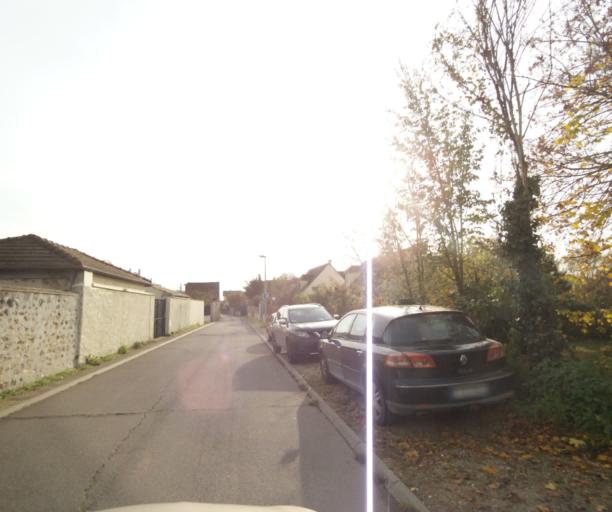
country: FR
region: Ile-de-France
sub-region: Departement des Yvelines
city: Triel-sur-Seine
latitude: 48.9732
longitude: 2.0052
